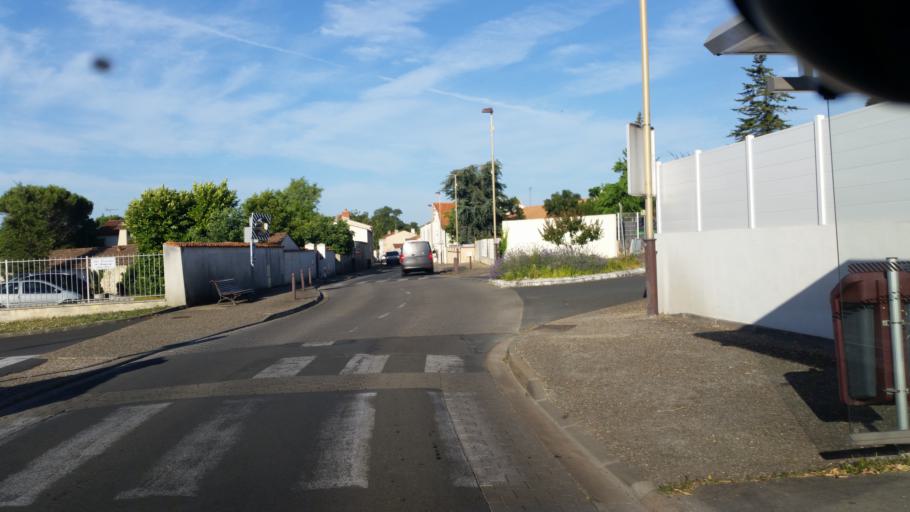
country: FR
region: Poitou-Charentes
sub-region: Departement de la Charente-Maritime
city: Perigny
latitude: 46.1689
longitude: -1.1087
